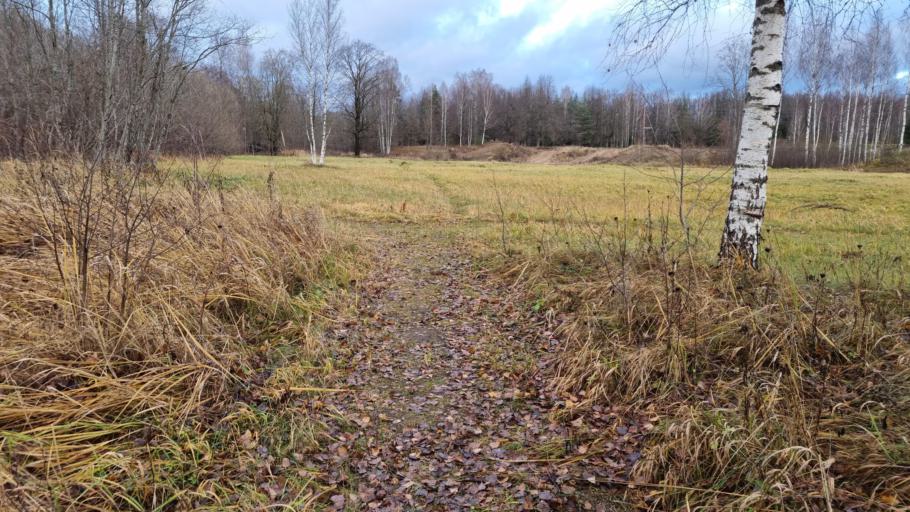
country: LV
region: Malpils
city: Malpils
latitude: 57.0043
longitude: 24.9648
